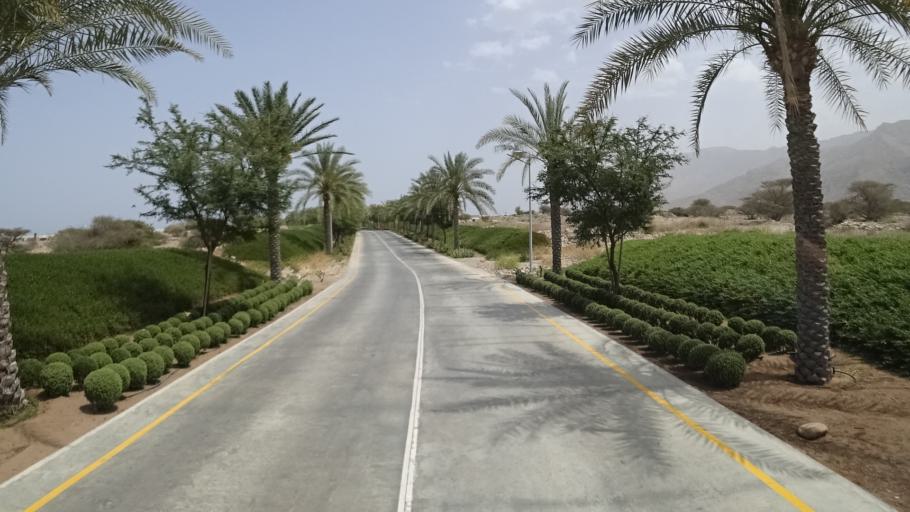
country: OM
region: Muhafazat Masqat
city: Muscat
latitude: 23.4142
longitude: 58.7828
